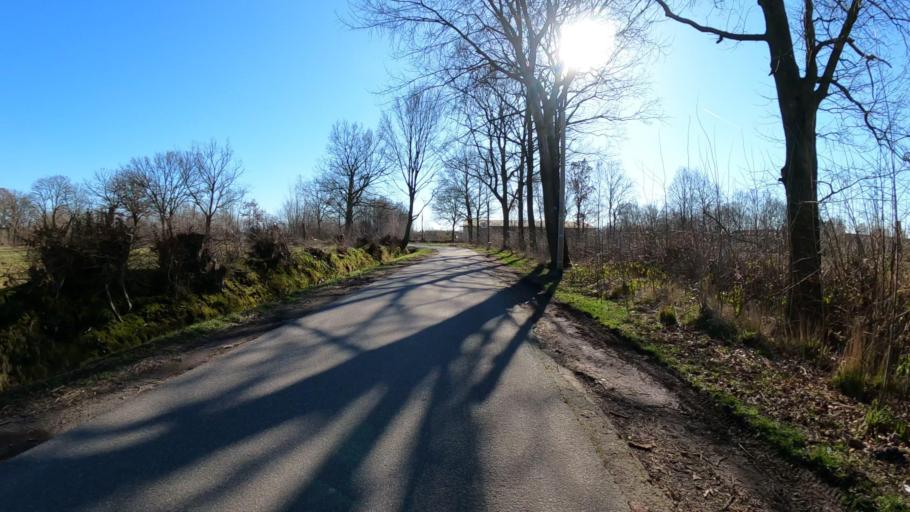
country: DE
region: Schleswig-Holstein
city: Kummerfeld
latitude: 53.6819
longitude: 9.7854
